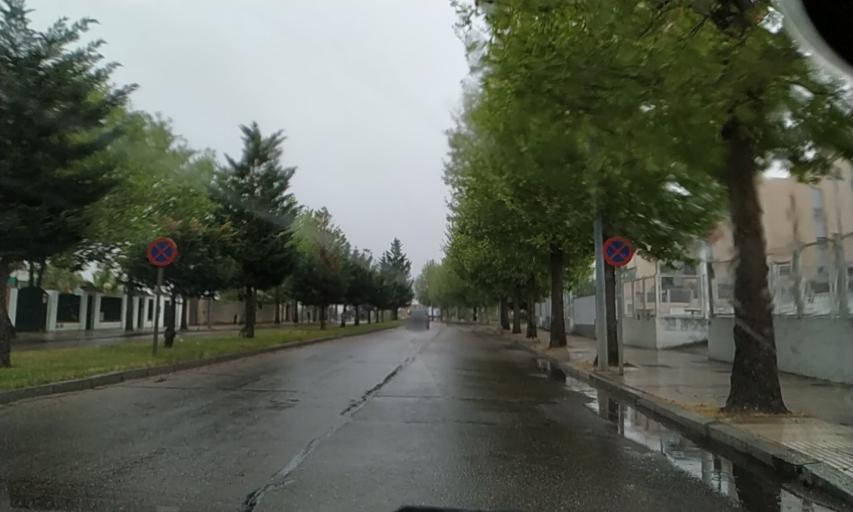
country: ES
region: Extremadura
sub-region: Provincia de Badajoz
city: Badajoz
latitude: 38.8637
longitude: -6.9728
